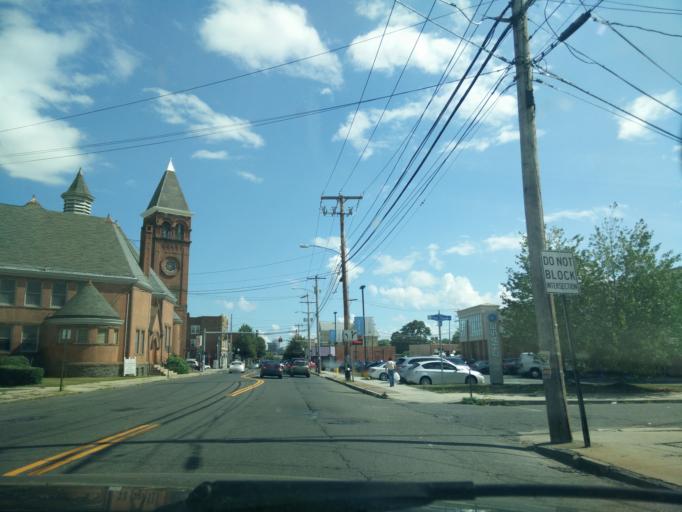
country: US
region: Connecticut
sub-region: Fairfield County
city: Bridgeport
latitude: 41.1926
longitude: -73.1976
